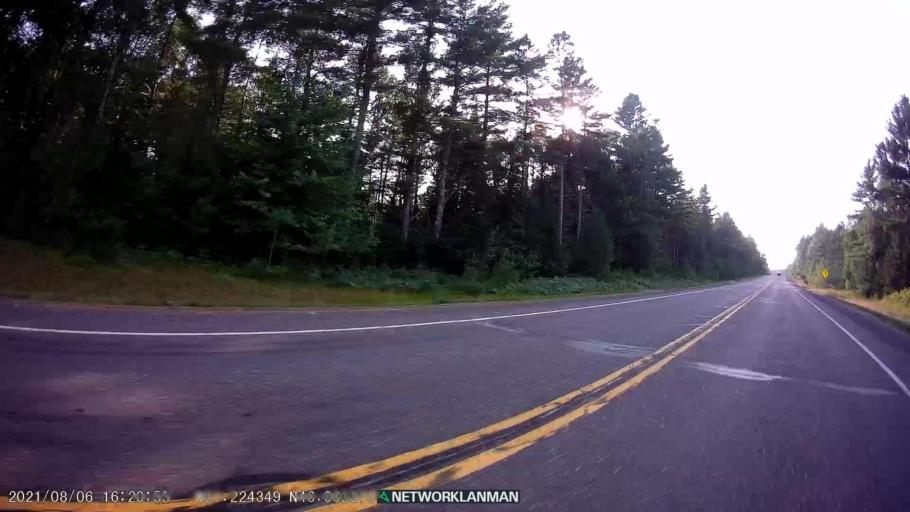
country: US
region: Wisconsin
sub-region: Sawyer County
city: Little Round Lake
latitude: 46.0657
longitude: -91.2249
